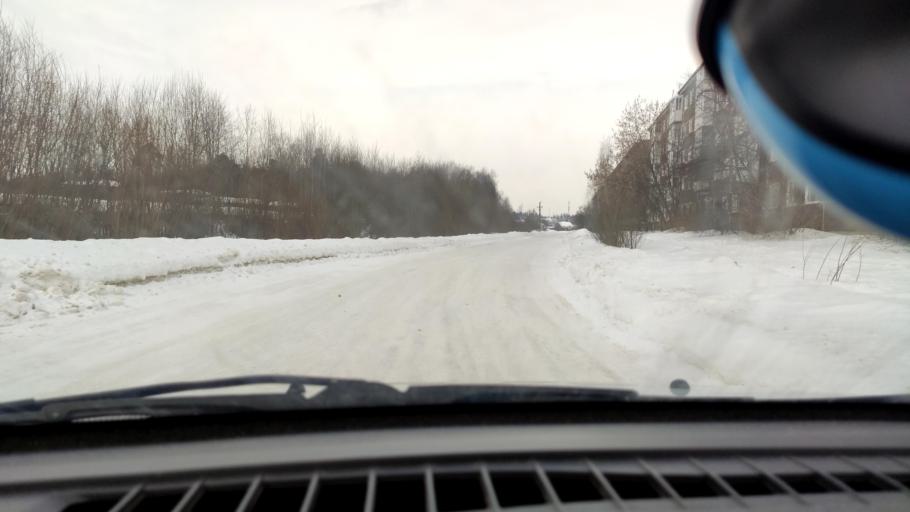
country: RU
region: Perm
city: Overyata
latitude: 58.0765
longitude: 55.8704
